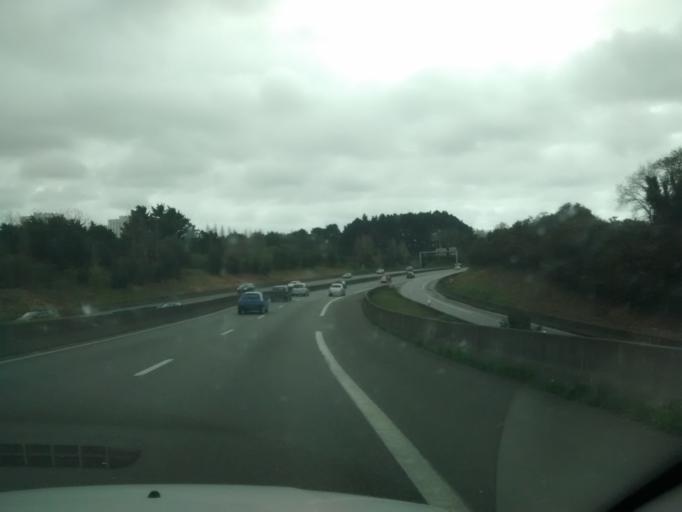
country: FR
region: Brittany
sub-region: Departement du Morbihan
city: Lorient
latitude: 47.7701
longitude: -3.3792
